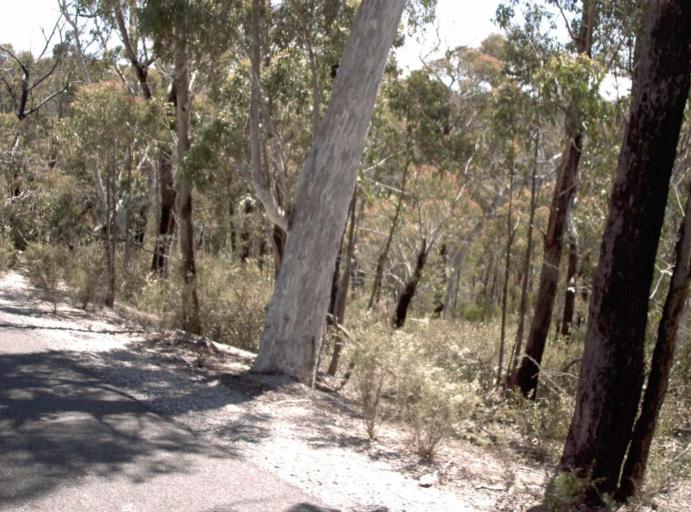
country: AU
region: New South Wales
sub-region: Snowy River
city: Jindabyne
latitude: -37.1215
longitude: 148.2467
